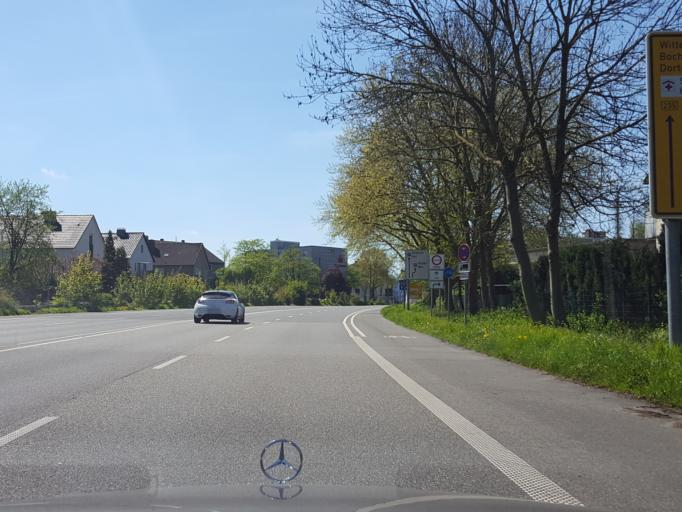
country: DE
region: North Rhine-Westphalia
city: Castrop-Rauxel
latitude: 51.5567
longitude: 7.3135
